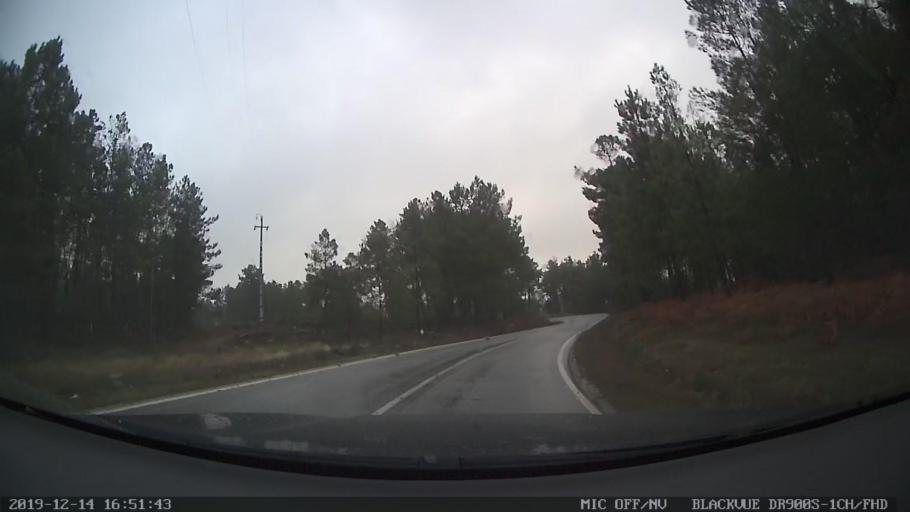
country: PT
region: Vila Real
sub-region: Murca
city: Murca
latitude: 41.4251
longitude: -7.5045
